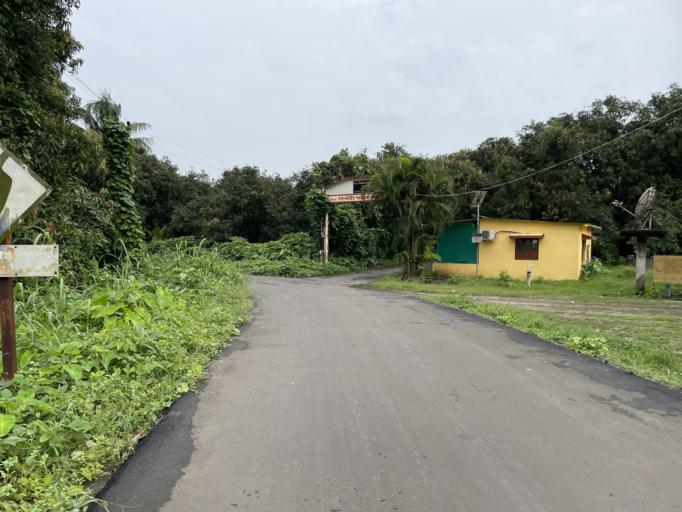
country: IN
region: Gujarat
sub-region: Valsad
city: Pardi
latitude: 20.4516
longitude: 72.9350
